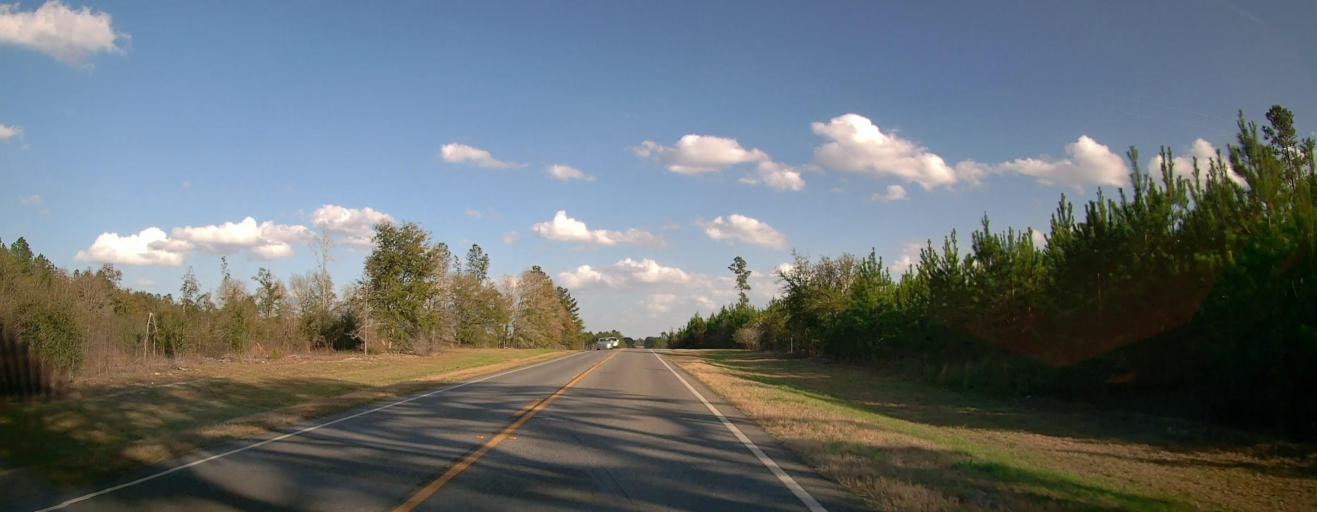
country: US
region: Georgia
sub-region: Tattnall County
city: Reidsville
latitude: 32.1236
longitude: -82.2026
